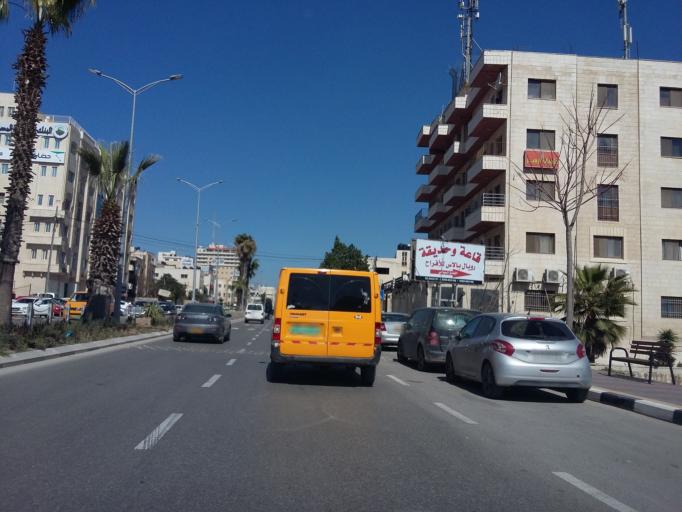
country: PS
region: West Bank
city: Ramallah
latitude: 31.8894
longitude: 35.2162
